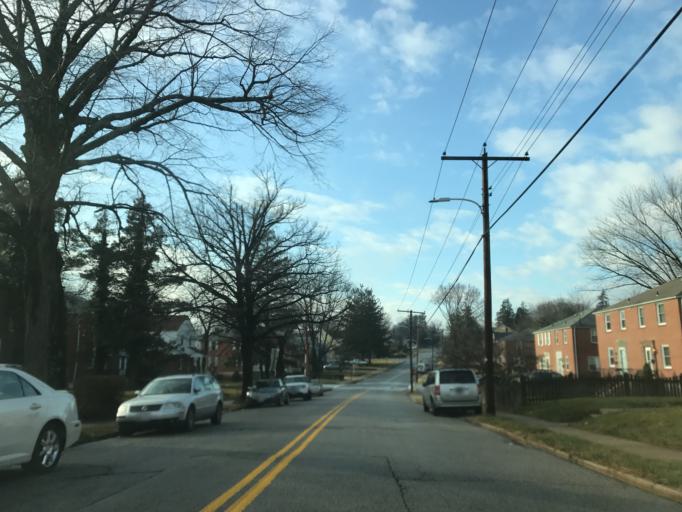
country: US
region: Maryland
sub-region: Baltimore County
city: Parkville
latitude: 39.3536
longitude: -76.5459
